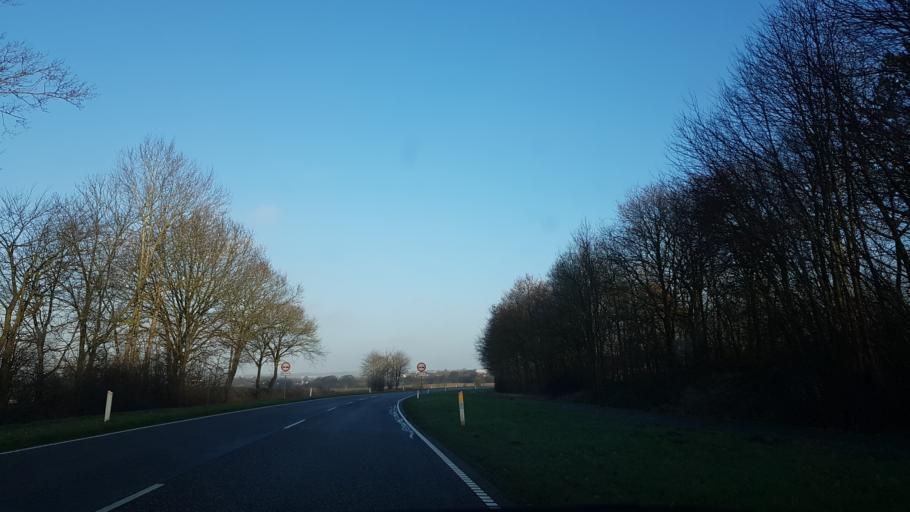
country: DK
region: South Denmark
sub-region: Haderslev Kommune
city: Haderslev
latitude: 55.2225
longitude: 9.4740
